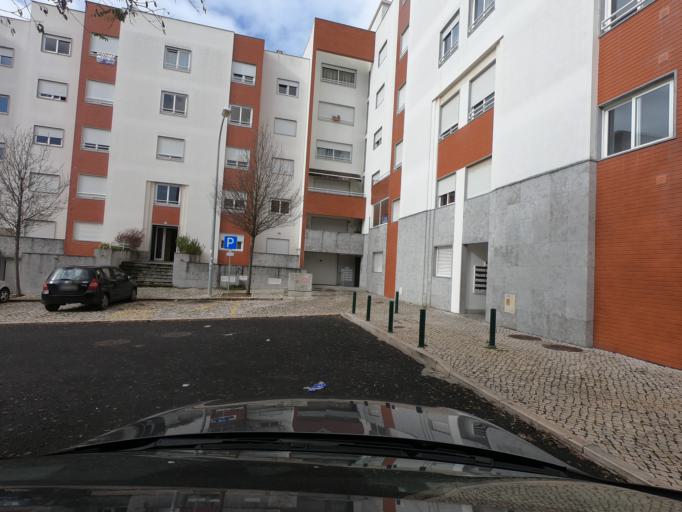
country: PT
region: Lisbon
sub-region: Cascais
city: Sao Domingos de Rana
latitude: 38.7096
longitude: -9.3279
